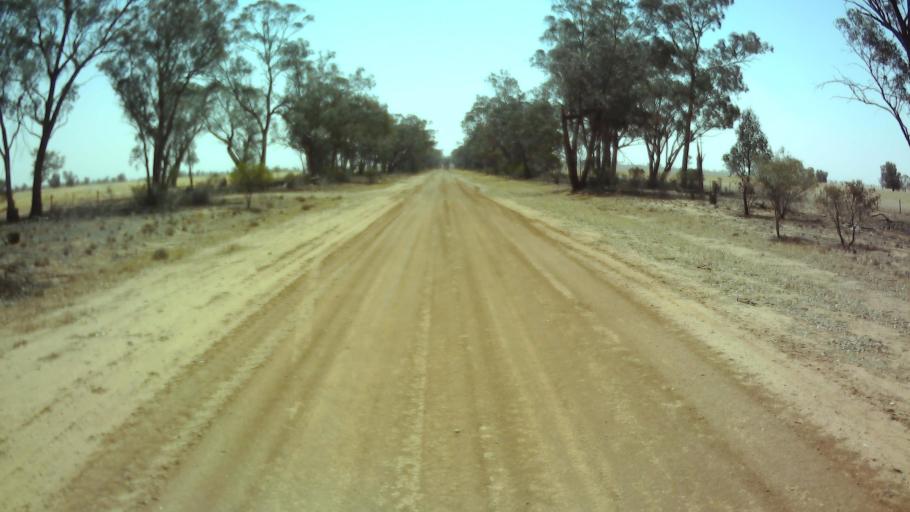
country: AU
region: New South Wales
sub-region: Weddin
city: Grenfell
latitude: -33.9261
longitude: 147.7891
